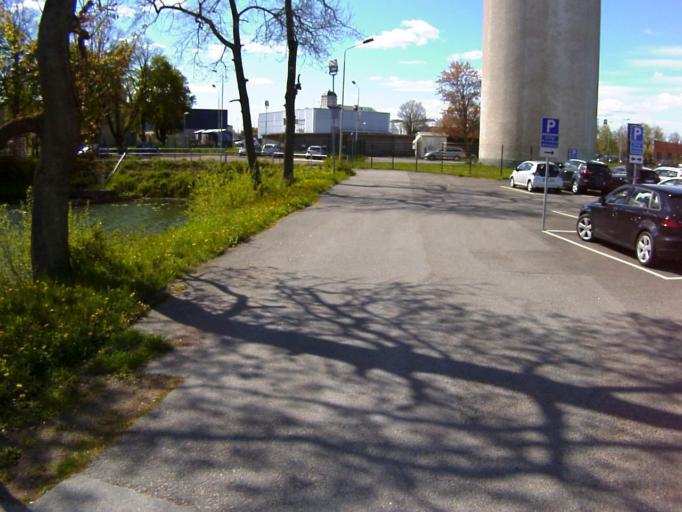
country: SE
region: Skane
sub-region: Kristianstads Kommun
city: Kristianstad
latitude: 56.0350
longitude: 14.1508
